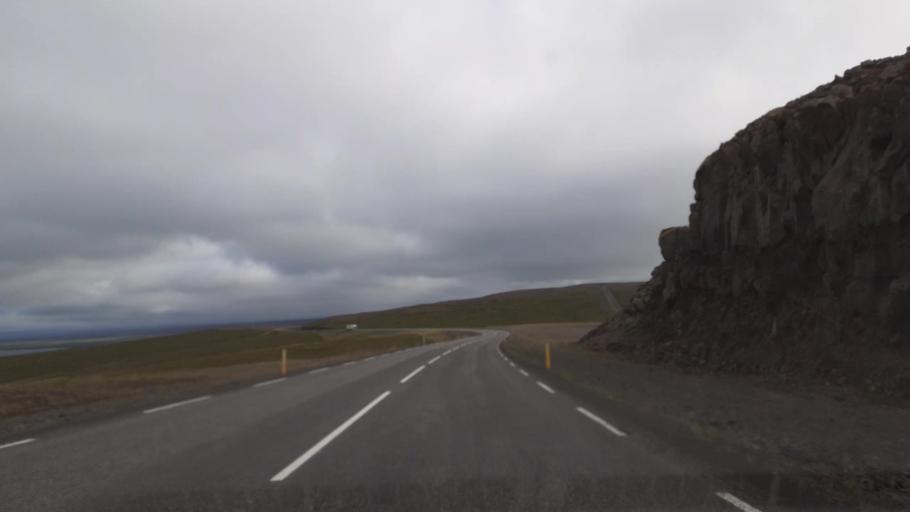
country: IS
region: Northeast
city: Husavik
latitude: 66.1456
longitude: -16.9675
